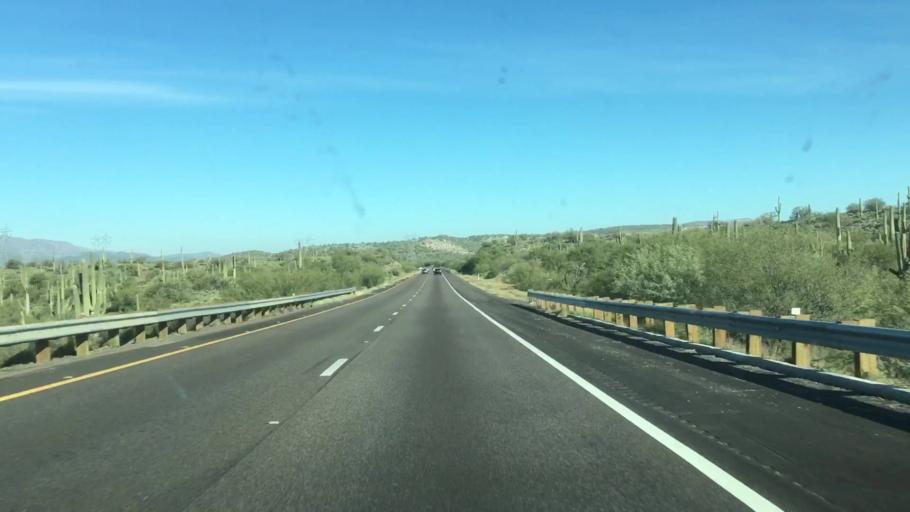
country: US
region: Arizona
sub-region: Yavapai County
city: Black Canyon City
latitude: 33.9997
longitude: -112.1330
